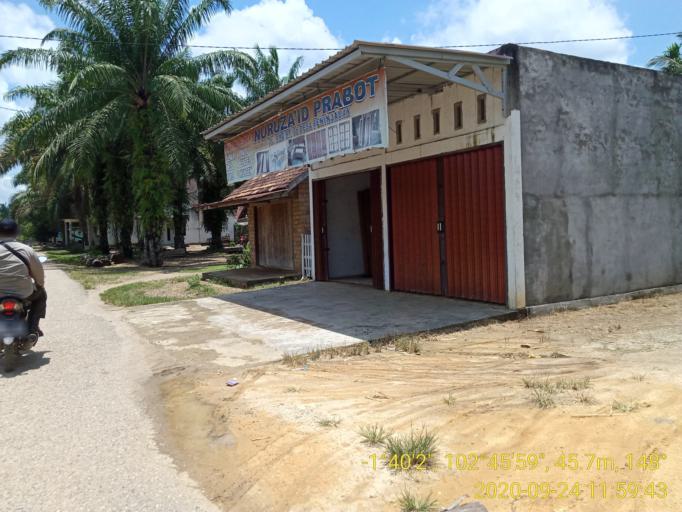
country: ID
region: Jambi
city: Sungaibengkal
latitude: -1.6674
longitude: 102.7664
